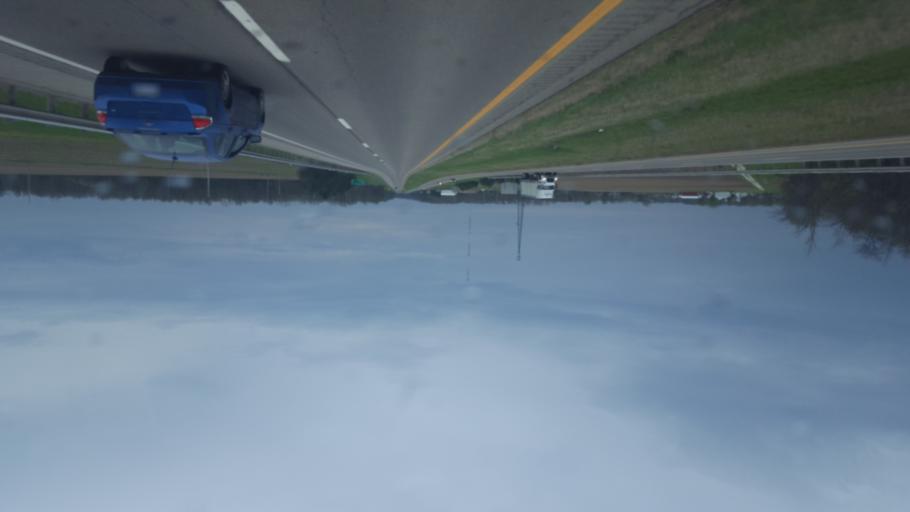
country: US
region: Ohio
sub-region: Wyandot County
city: Carey
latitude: 40.9370
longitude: -83.3920
